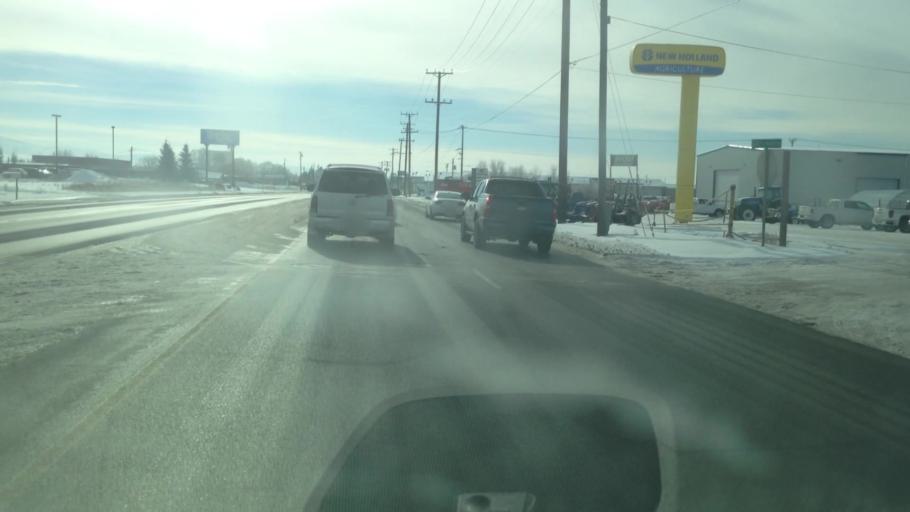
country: US
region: Idaho
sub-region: Bonneville County
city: Idaho Falls
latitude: 43.5247
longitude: -112.0236
